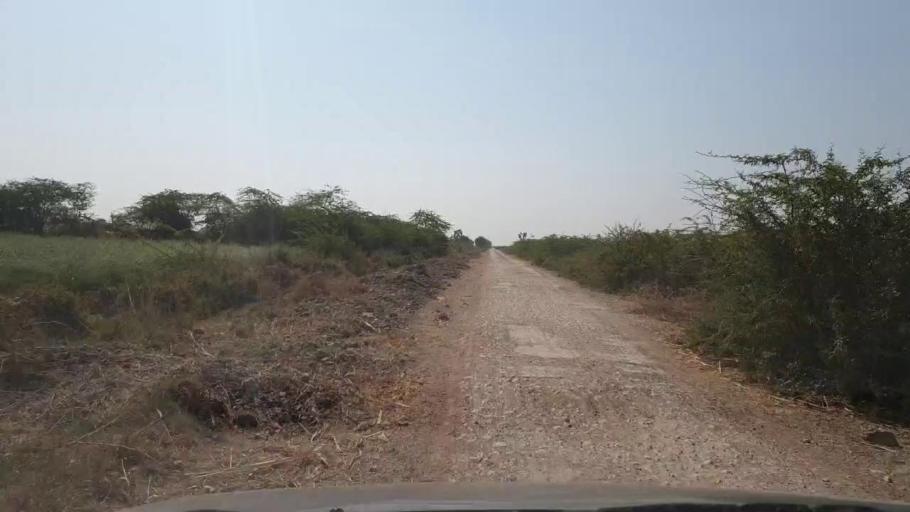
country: PK
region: Sindh
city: Digri
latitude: 25.2019
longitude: 69.2286
